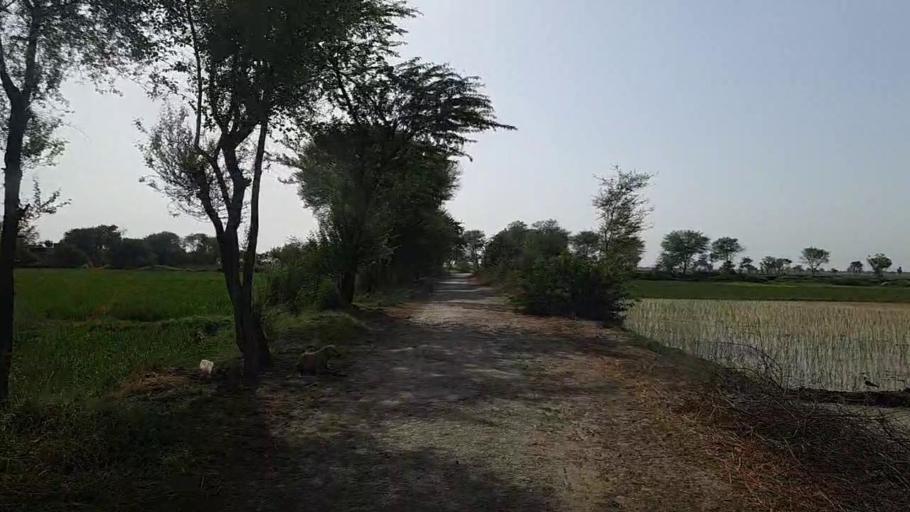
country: PK
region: Sindh
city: Sita Road
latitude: 27.0879
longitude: 67.8476
